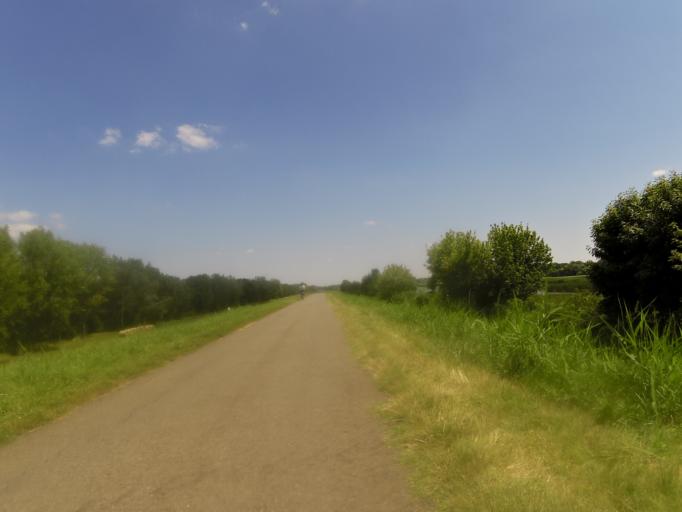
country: HU
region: Heves
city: Kiskore
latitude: 47.5101
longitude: 20.5487
